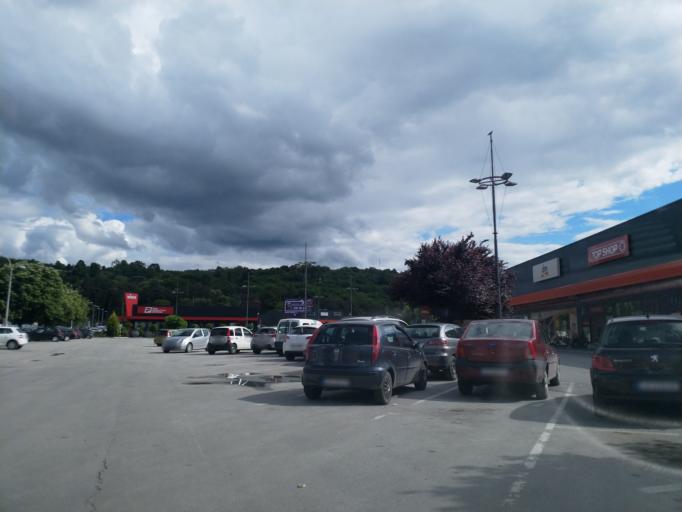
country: RS
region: Central Serbia
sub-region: Pomoravski Okrug
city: Jagodina
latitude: 43.9676
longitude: 21.2648
